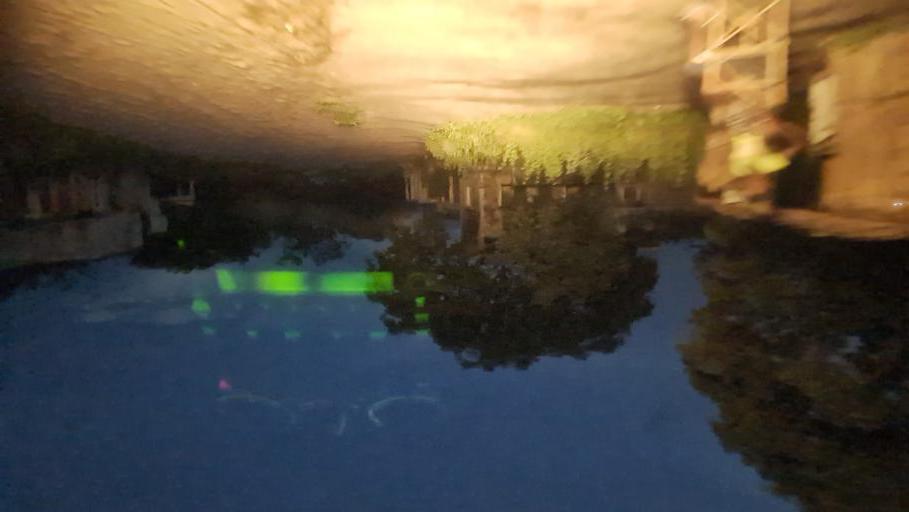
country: MZ
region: Nampula
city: Nampula
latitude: -14.6620
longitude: 39.8381
